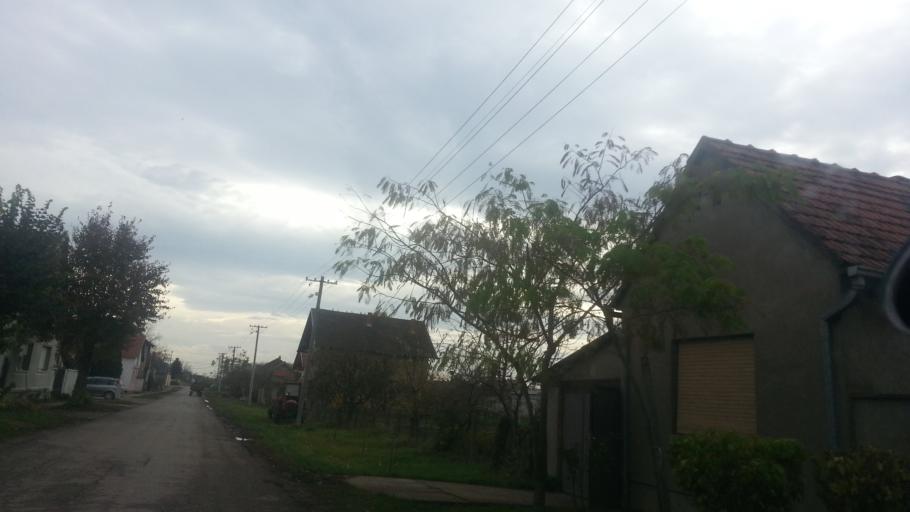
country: RS
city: Golubinci
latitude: 44.9873
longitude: 20.0586
